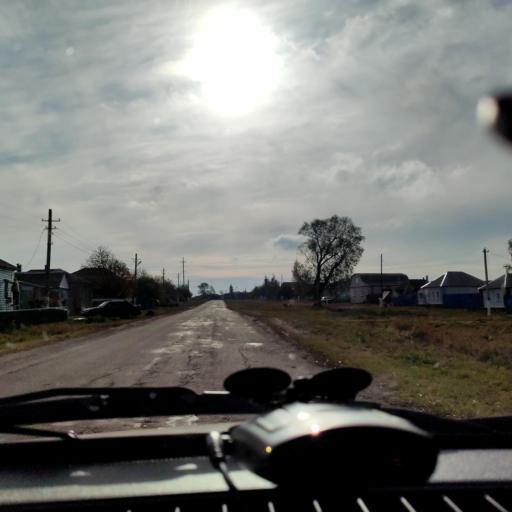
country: RU
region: Voronezj
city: Rossosh'
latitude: 51.2110
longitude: 38.7612
